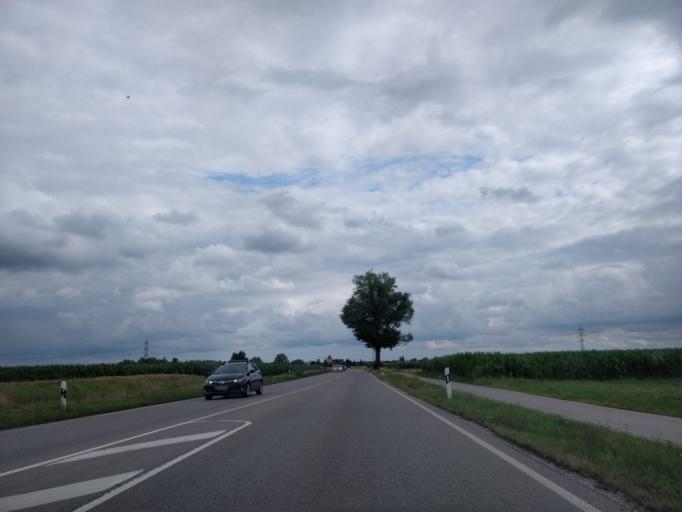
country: DE
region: Bavaria
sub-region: Swabia
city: Kissing
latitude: 48.2925
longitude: 10.9659
